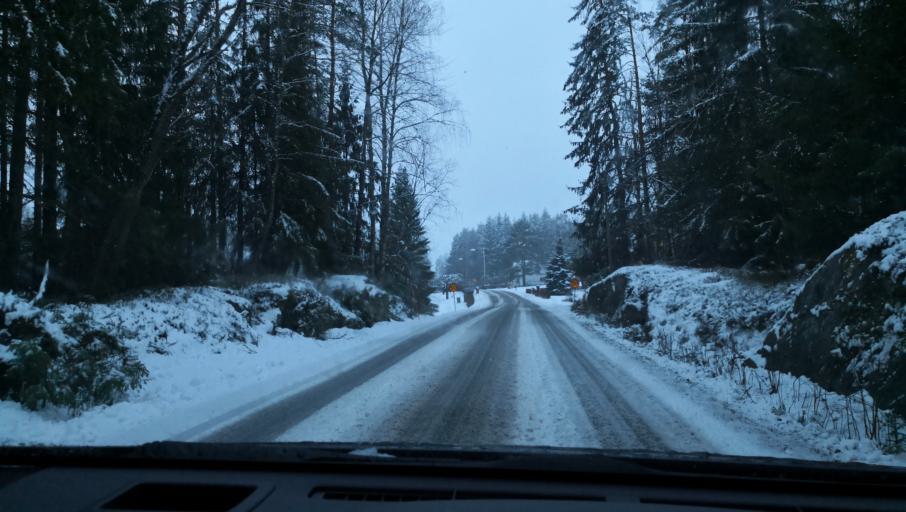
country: SE
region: Vaestmanland
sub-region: Kopings Kommun
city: Kolsva
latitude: 59.6035
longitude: 15.8611
